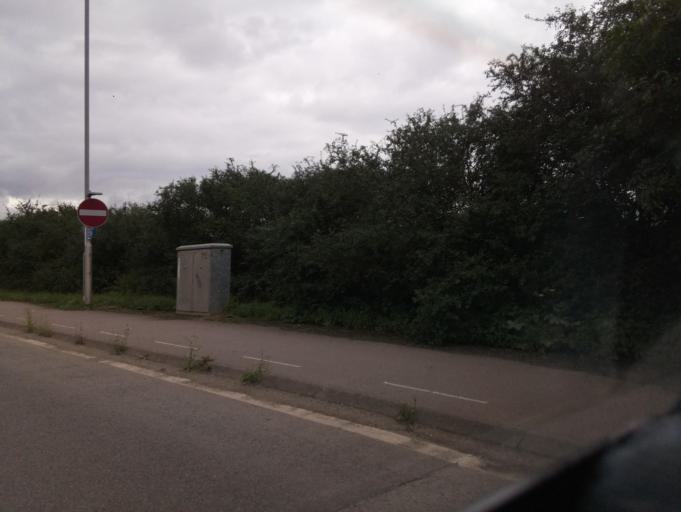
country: GB
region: England
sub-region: Nottinghamshire
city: Bingham
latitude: 52.9507
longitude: -0.9775
